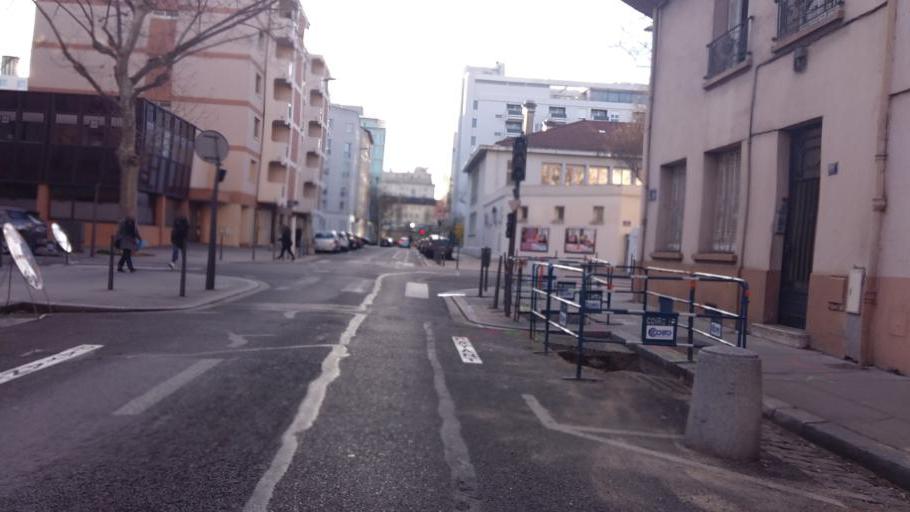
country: FR
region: Rhone-Alpes
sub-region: Departement du Rhone
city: Villeurbanne
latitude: 45.7652
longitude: 4.8640
